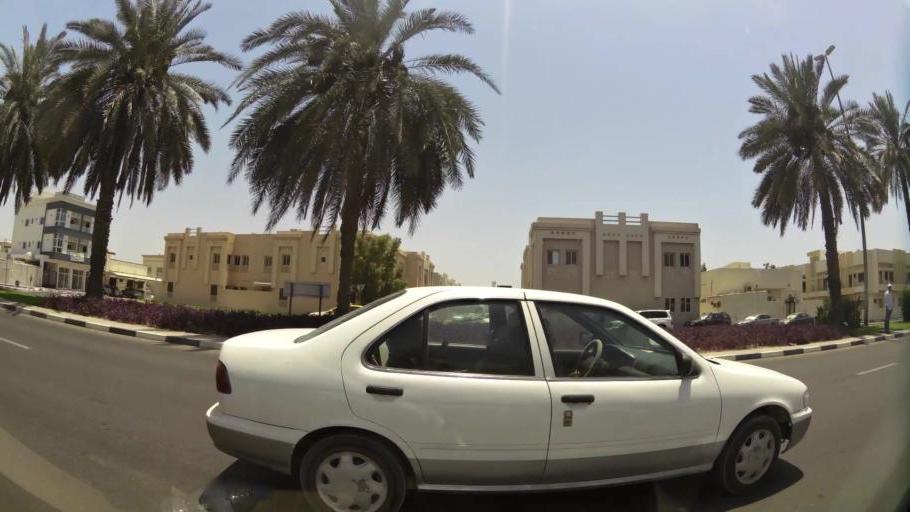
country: AE
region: Ash Shariqah
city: Sharjah
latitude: 25.2917
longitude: 55.3288
